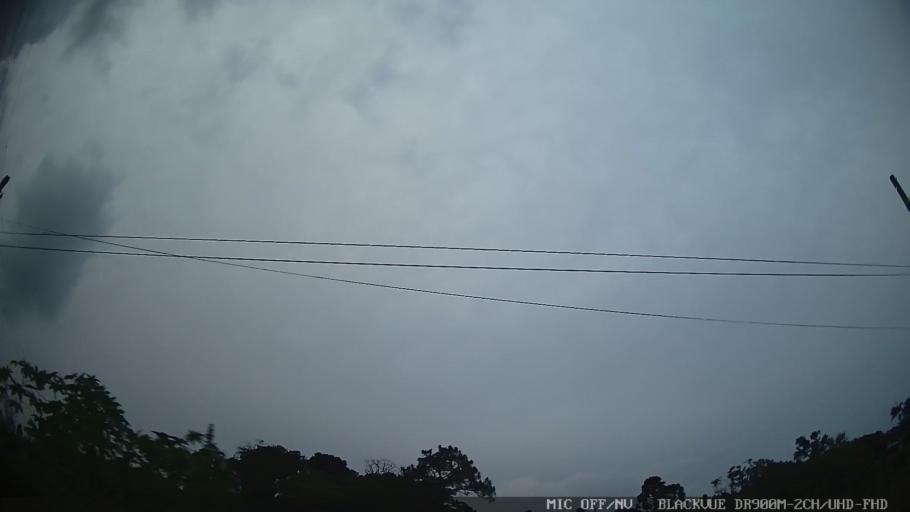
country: BR
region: Sao Paulo
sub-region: Braganca Paulista
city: Braganca Paulista
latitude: -22.9489
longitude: -46.5871
